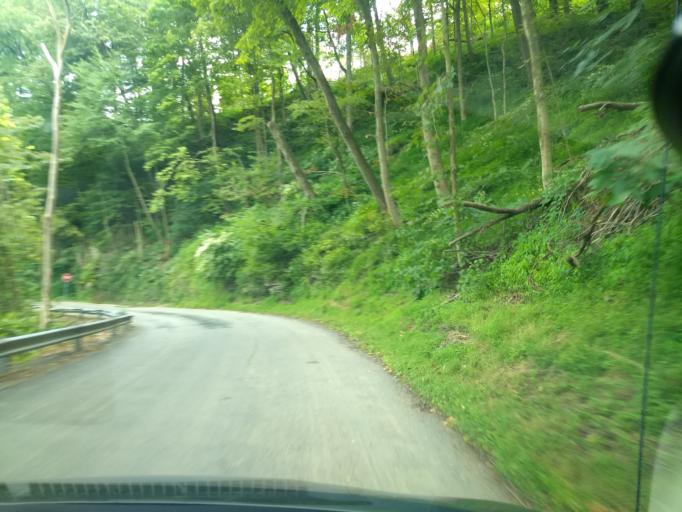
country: US
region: Pennsylvania
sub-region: Westmoreland County
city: Murrysville
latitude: 40.4221
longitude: -79.7260
